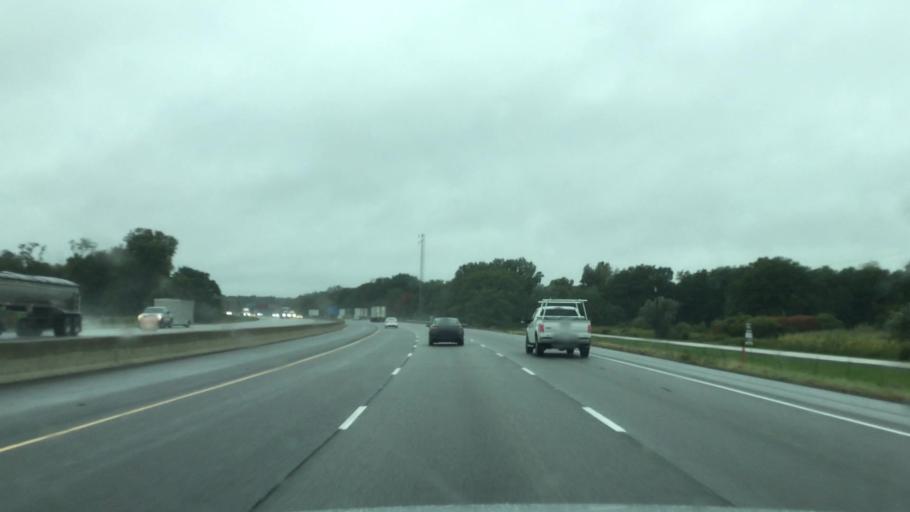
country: US
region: Indiana
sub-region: Porter County
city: Burns Harbor
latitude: 41.6071
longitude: -87.1309
